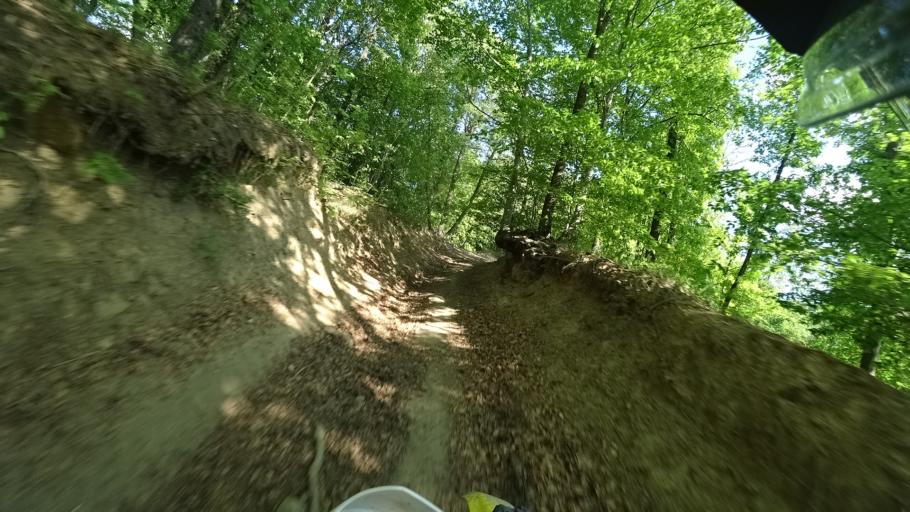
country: HR
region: Zagrebacka
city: Jablanovec
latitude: 45.8768
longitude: 15.8754
